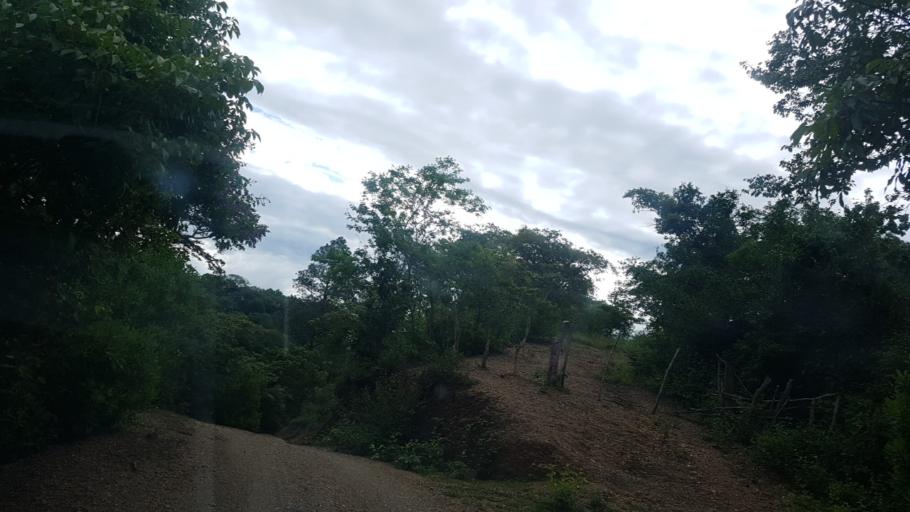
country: NI
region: Nueva Segovia
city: Ocotal
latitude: 13.5960
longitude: -86.4196
